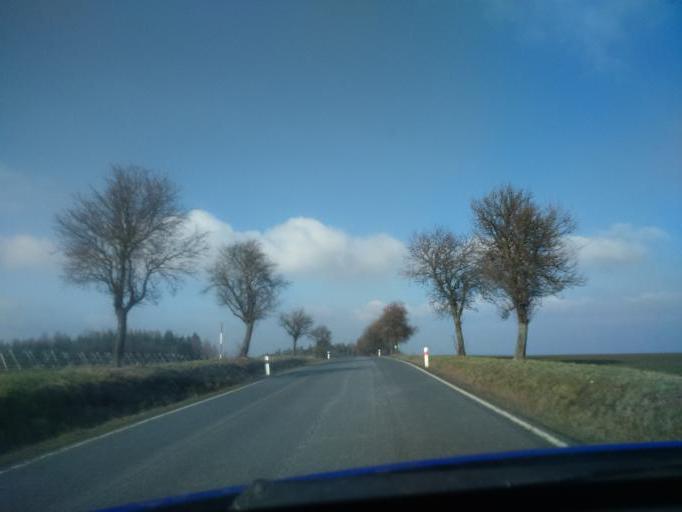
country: CZ
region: Plzensky
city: Horsovsky Tyn
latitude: 49.4907
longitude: 12.9452
